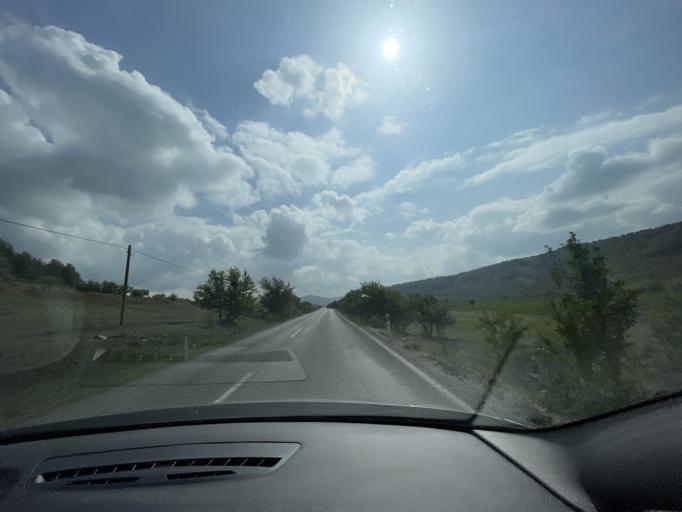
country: TR
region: Denizli
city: Acipayam
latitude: 37.5106
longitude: 29.4496
